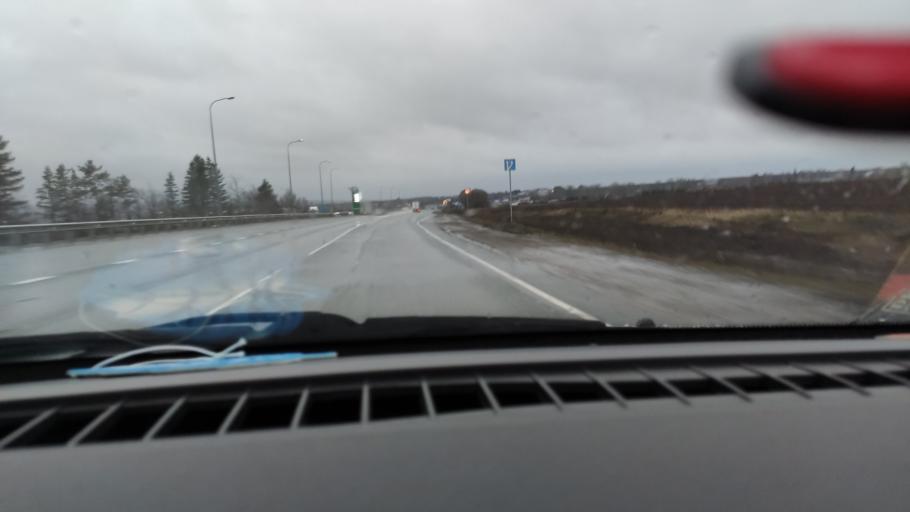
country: RU
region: Tatarstan
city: Mendeleyevsk
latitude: 56.0350
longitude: 52.3826
